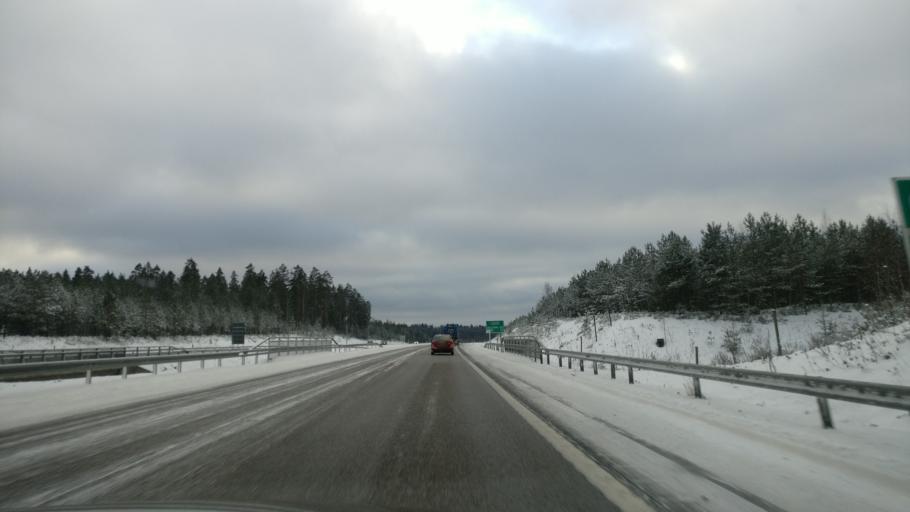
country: FI
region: Paijanne Tavastia
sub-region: Lahti
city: Nastola
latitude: 61.1066
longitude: 25.9155
